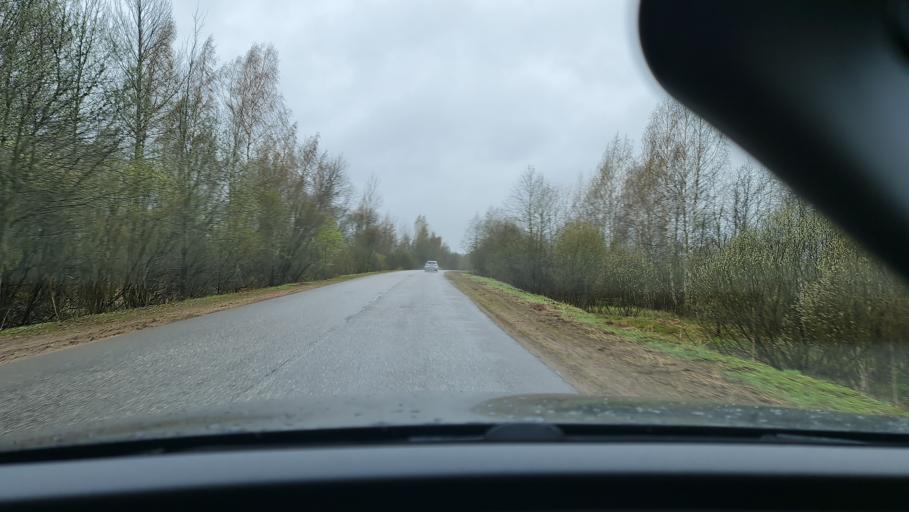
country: RU
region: Novgorod
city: Kresttsy
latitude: 57.9764
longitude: 32.7350
